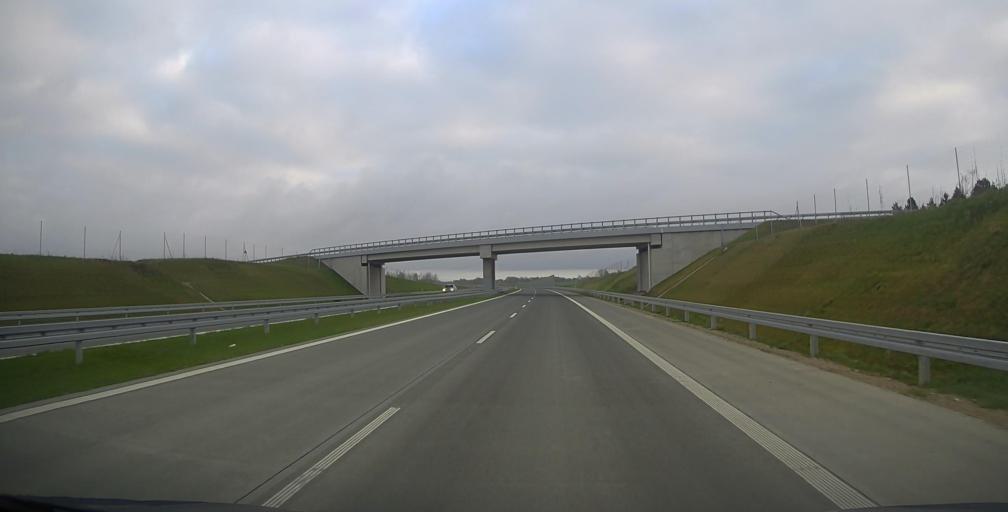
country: PL
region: Podlasie
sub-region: Powiat suwalski
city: Raczki
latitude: 53.9240
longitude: 22.7496
